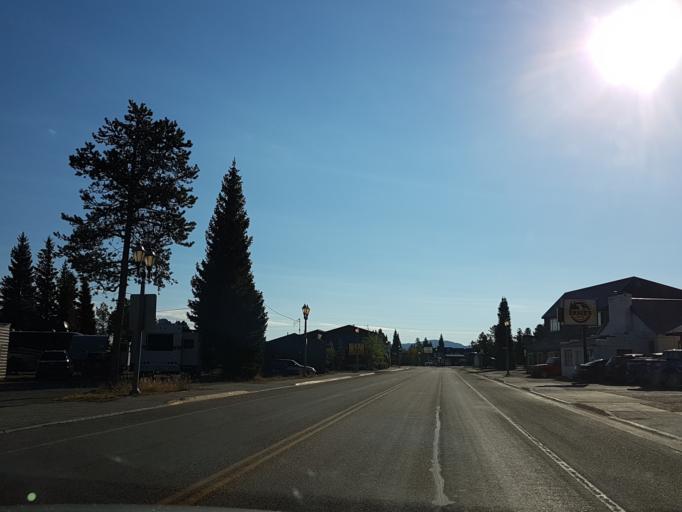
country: US
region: Montana
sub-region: Gallatin County
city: West Yellowstone
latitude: 44.6628
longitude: -111.1077
